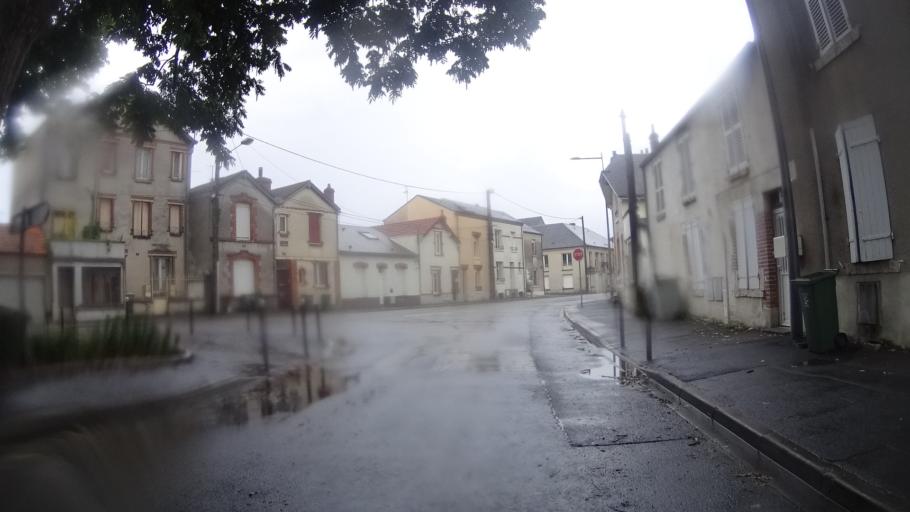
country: FR
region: Centre
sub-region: Departement du Loiret
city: Saint-Jean-le-Blanc
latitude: 47.8940
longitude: 1.9134
